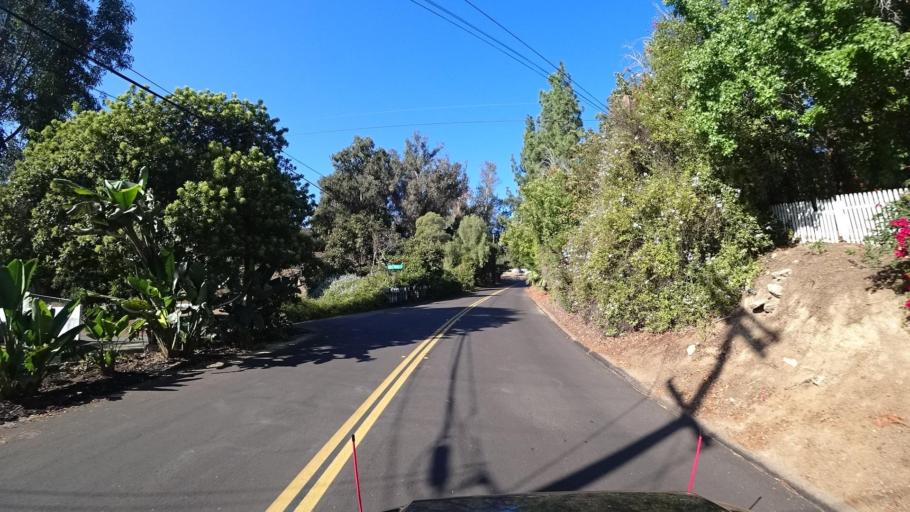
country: US
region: California
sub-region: San Diego County
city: Casa de Oro-Mount Helix
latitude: 32.7701
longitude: -116.9783
